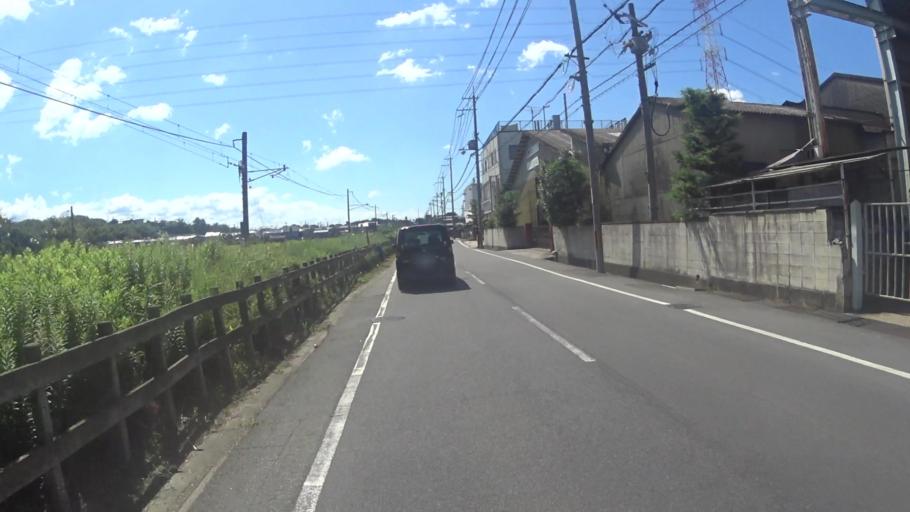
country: JP
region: Kyoto
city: Tanabe
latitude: 34.8060
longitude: 135.8067
